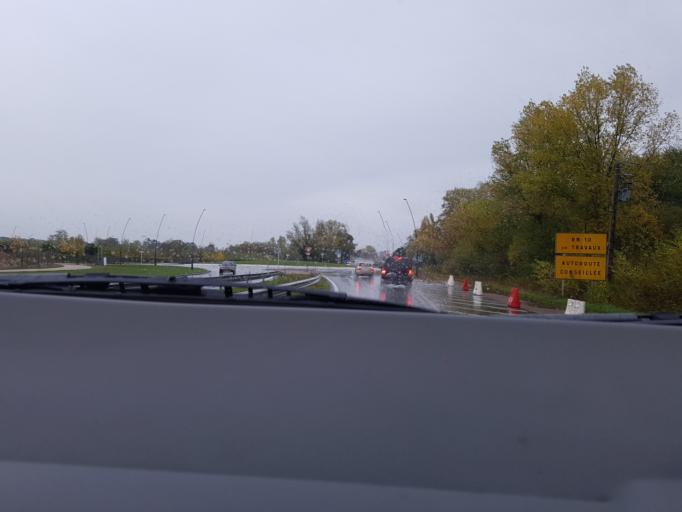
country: FR
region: Aquitaine
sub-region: Departement de la Gironde
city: Saint-Gervais
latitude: 45.0087
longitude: -0.4332
